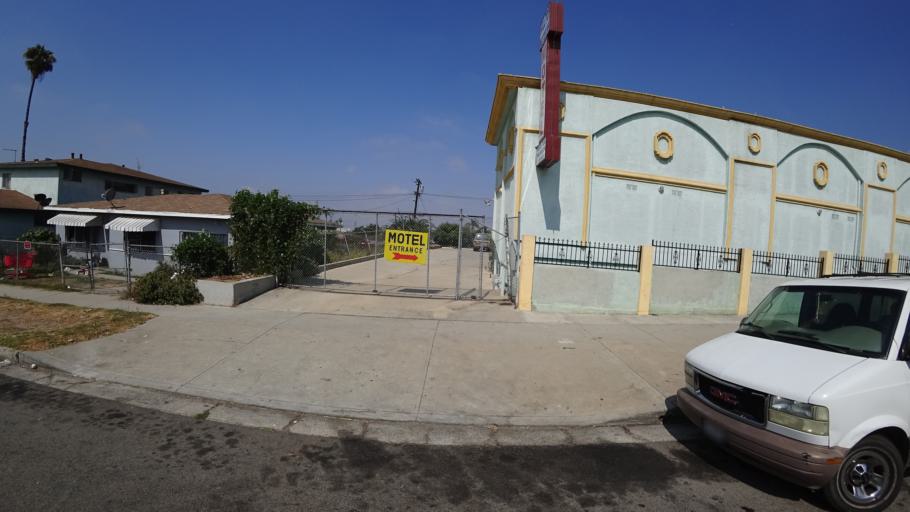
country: US
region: California
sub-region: Los Angeles County
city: Westmont
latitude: 33.9395
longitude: -118.3091
